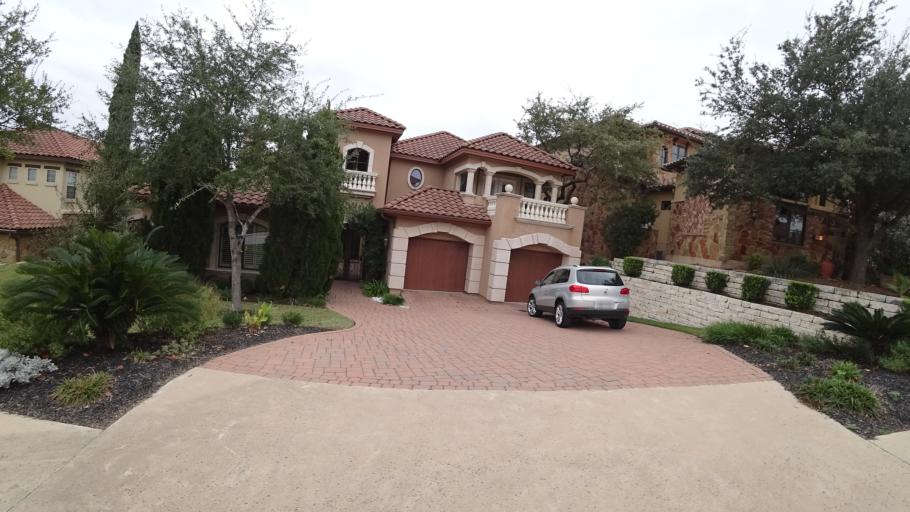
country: US
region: Texas
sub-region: Travis County
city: Bee Cave
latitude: 30.3191
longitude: -97.9171
